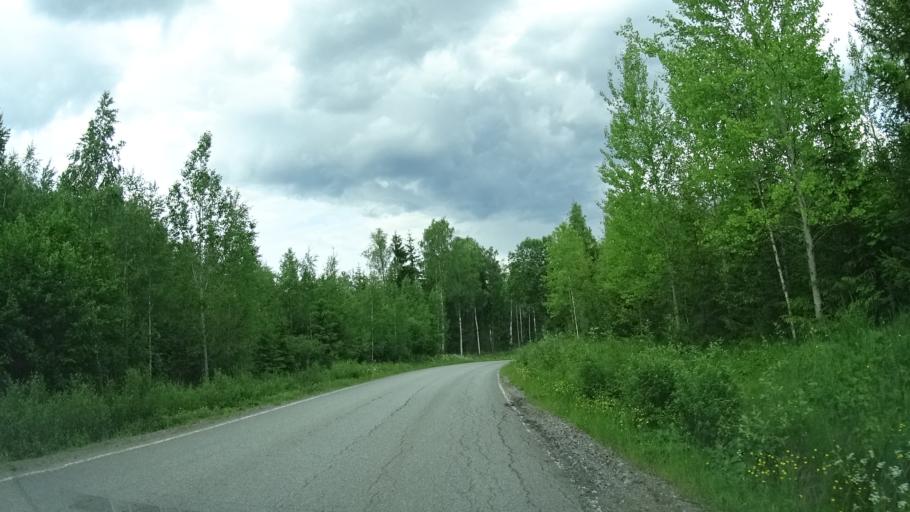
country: FI
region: Uusimaa
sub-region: Helsinki
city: Siuntio
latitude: 60.2001
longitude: 24.2315
